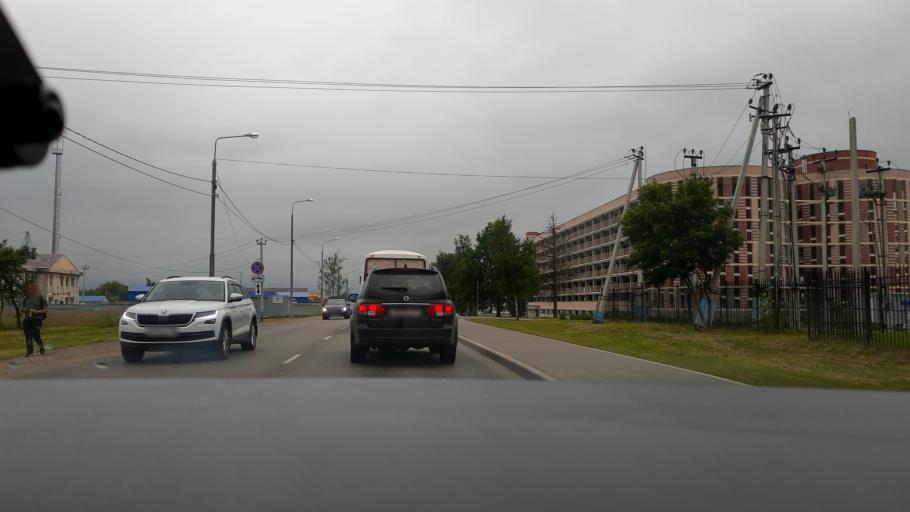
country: RU
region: Moskovskaya
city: Kokoshkino
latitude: 55.5435
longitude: 37.1551
